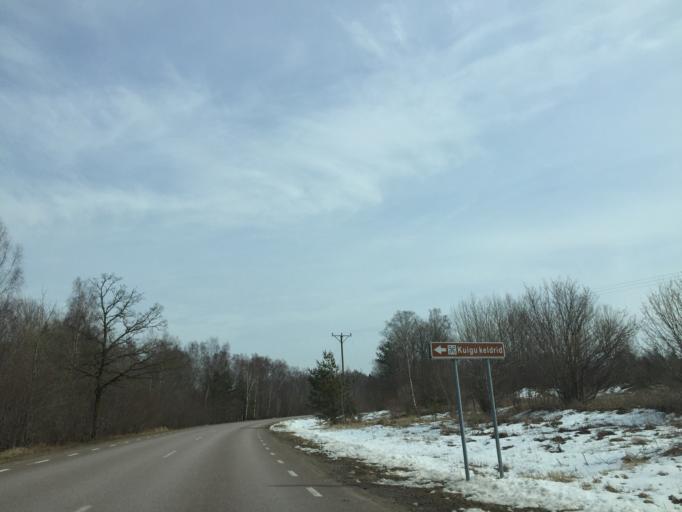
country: EE
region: Saare
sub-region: Kuressaare linn
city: Kuressaare
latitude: 58.3401
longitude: 22.4737
